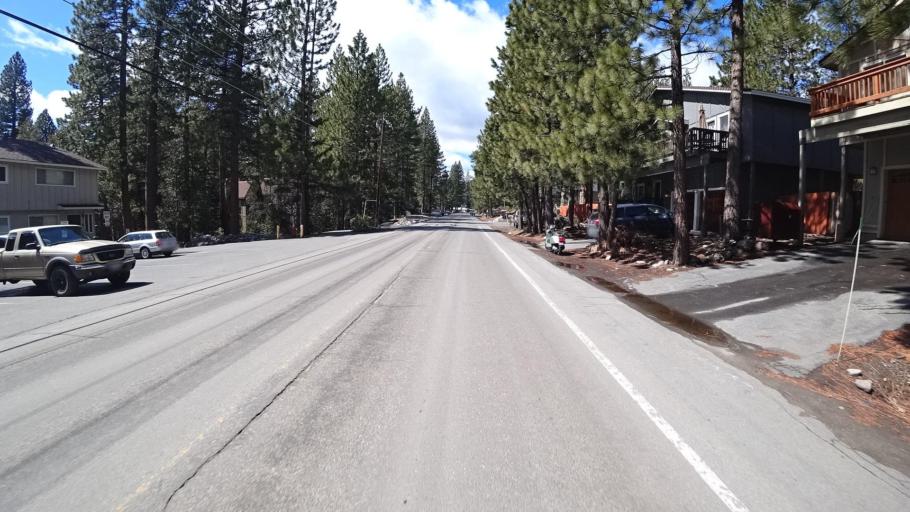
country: US
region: Nevada
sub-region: Washoe County
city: Incline Village
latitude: 39.2471
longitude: -119.9584
